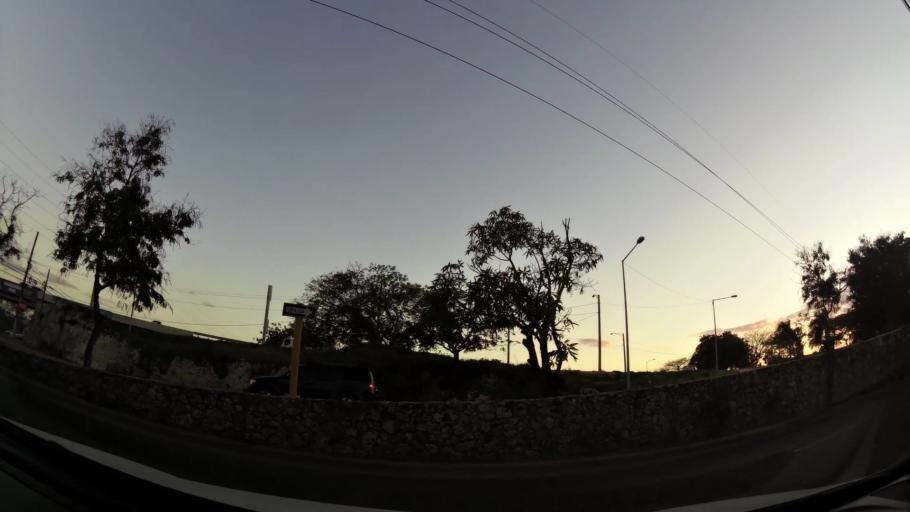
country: DO
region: Santo Domingo
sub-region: Santo Domingo
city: Santo Domingo Este
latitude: 18.4839
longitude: -69.8274
